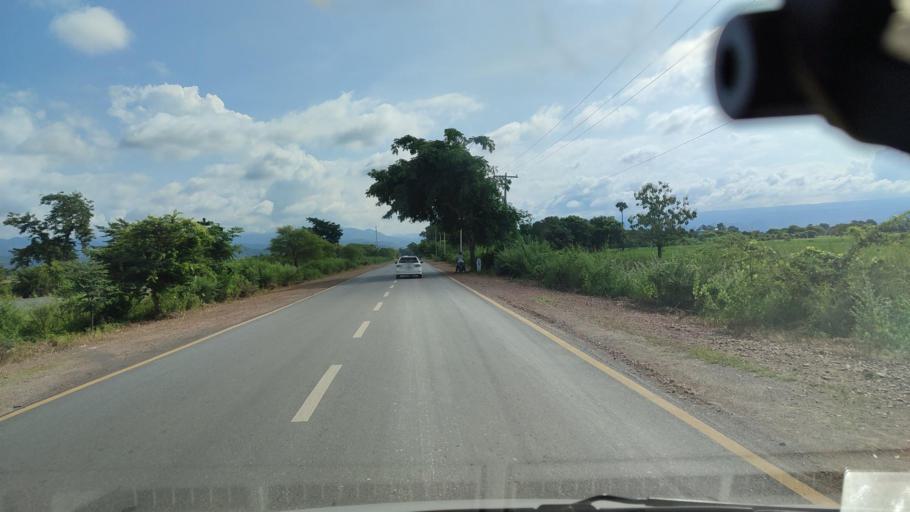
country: MM
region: Mandalay
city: Mandalay
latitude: 21.8692
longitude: 96.1706
